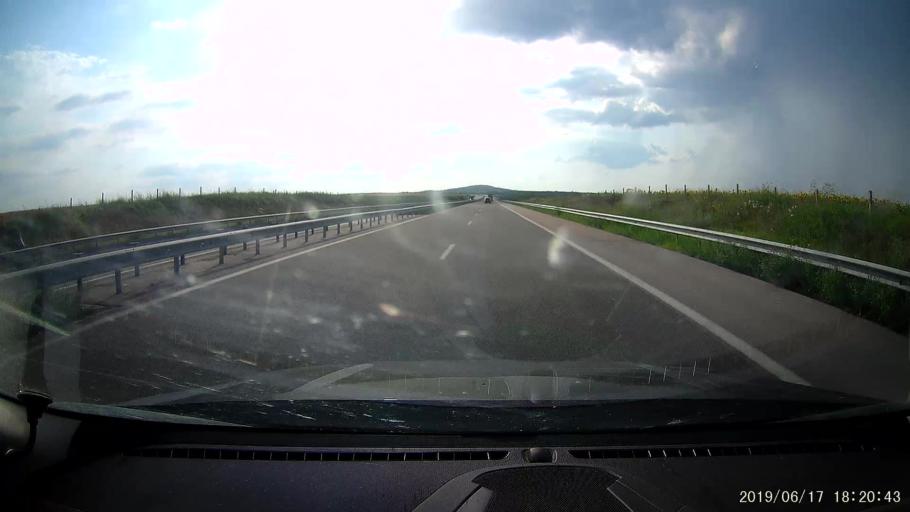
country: BG
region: Khaskovo
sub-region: Obshtina Simeonovgrad
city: Simeonovgrad
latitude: 41.9635
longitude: 25.8047
